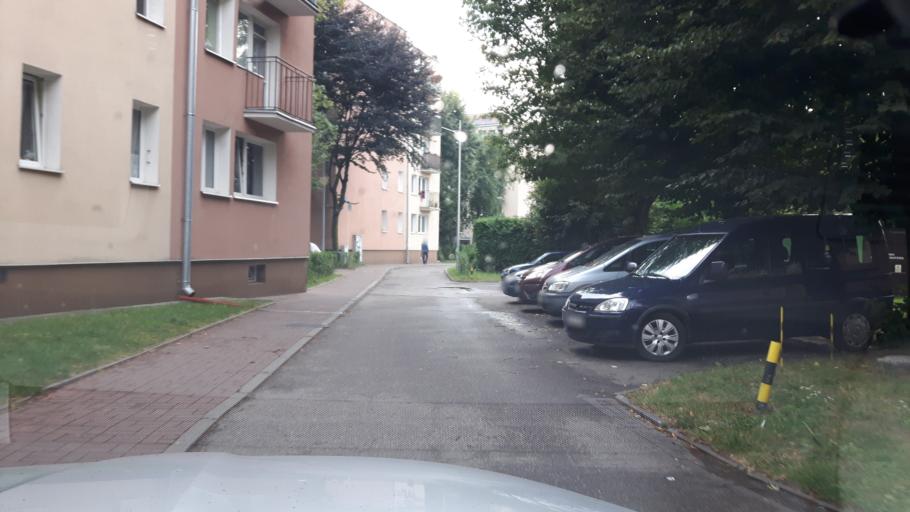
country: PL
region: Masovian Voivodeship
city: Zielonka
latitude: 52.3141
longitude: 21.1606
